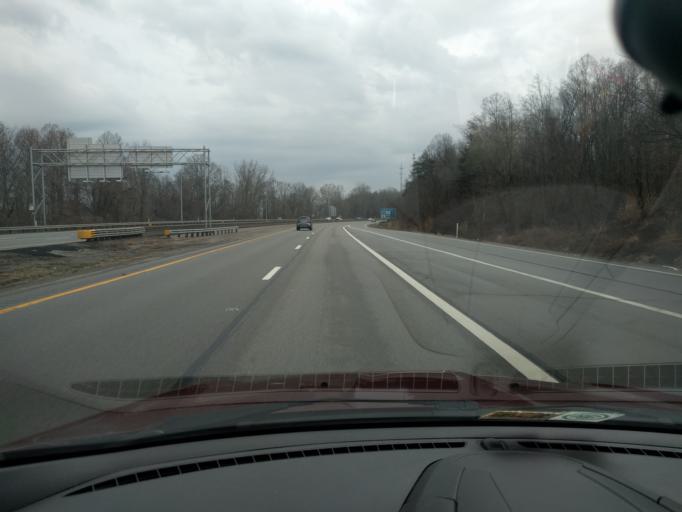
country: US
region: West Virginia
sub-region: Wood County
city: Williamstown
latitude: 39.3913
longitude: -81.4393
